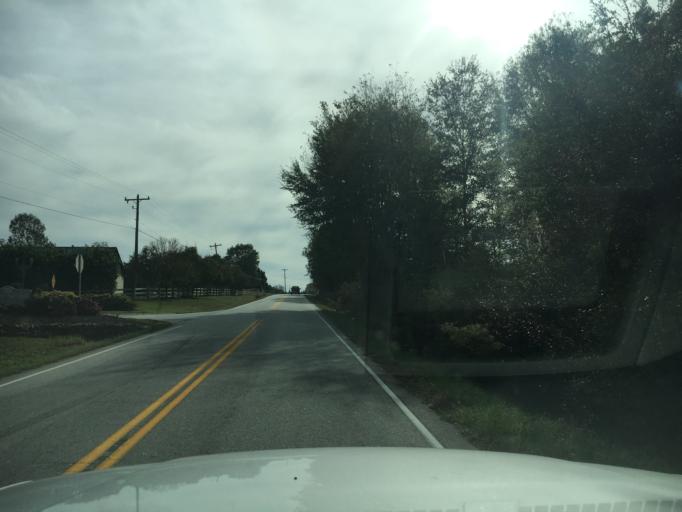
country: US
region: South Carolina
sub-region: Spartanburg County
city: Duncan
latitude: 34.9240
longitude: -82.1564
